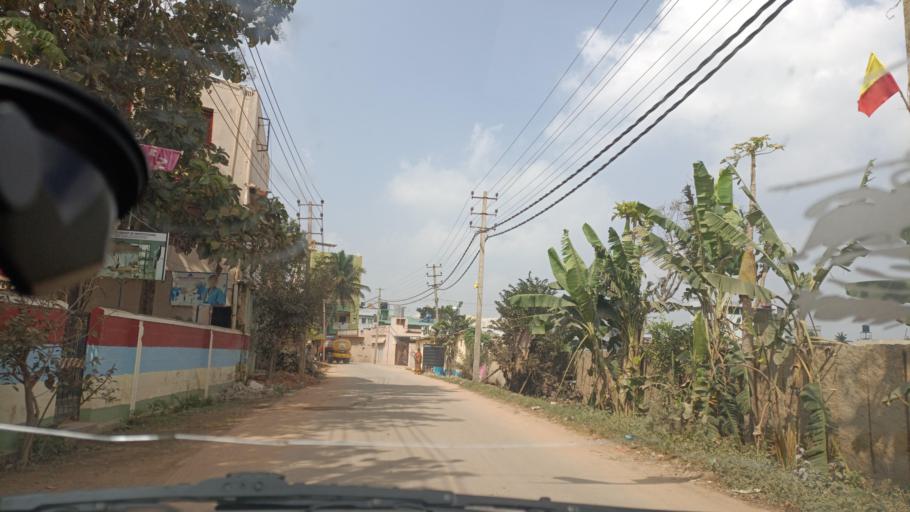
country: IN
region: Karnataka
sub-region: Bangalore Urban
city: Yelahanka
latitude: 13.1541
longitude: 77.6270
